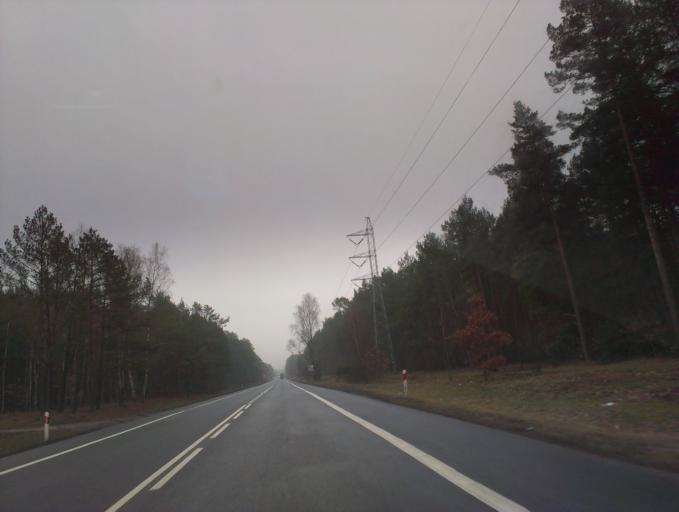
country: PL
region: Greater Poland Voivodeship
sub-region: Powiat pilski
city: Pila
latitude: 53.1789
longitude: 16.7740
